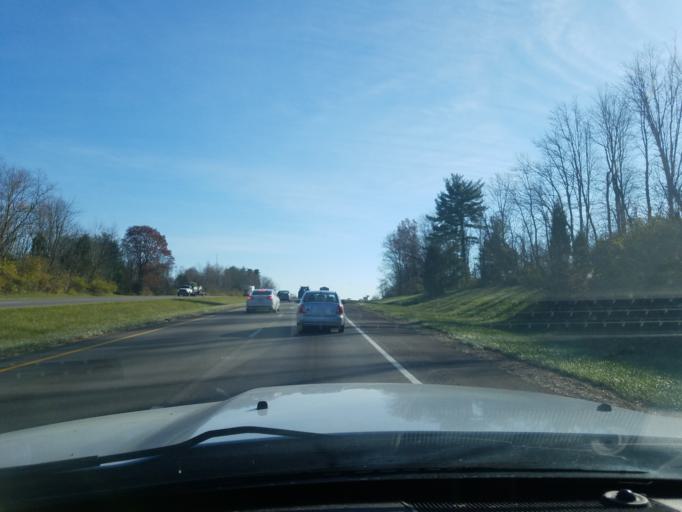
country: US
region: Ohio
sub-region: Clermont County
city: Batavia
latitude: 39.0854
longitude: -84.1596
